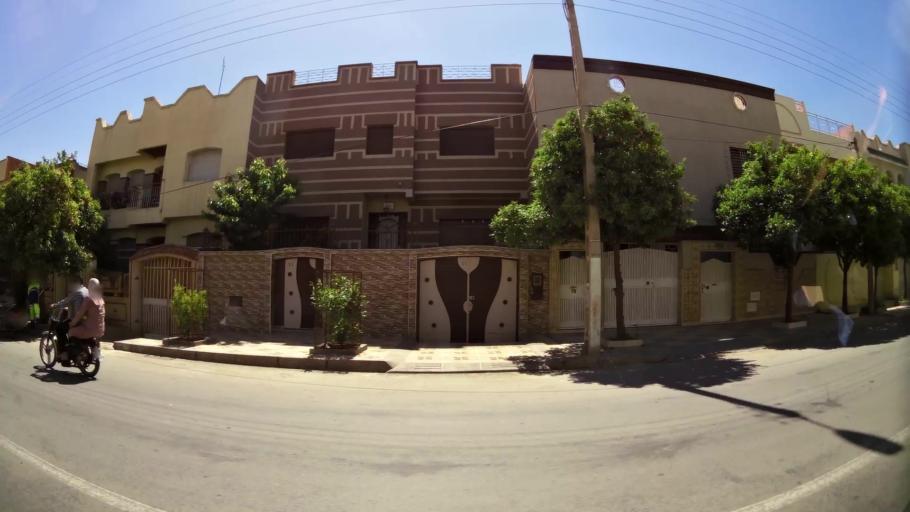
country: MA
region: Oriental
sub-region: Oujda-Angad
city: Oujda
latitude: 34.6641
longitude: -1.9286
